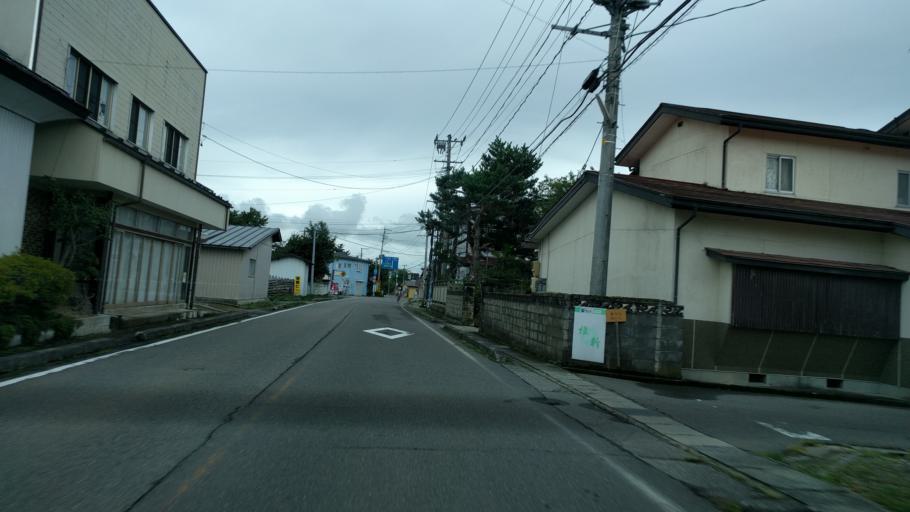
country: JP
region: Fukushima
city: Kitakata
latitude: 37.6056
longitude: 139.8505
